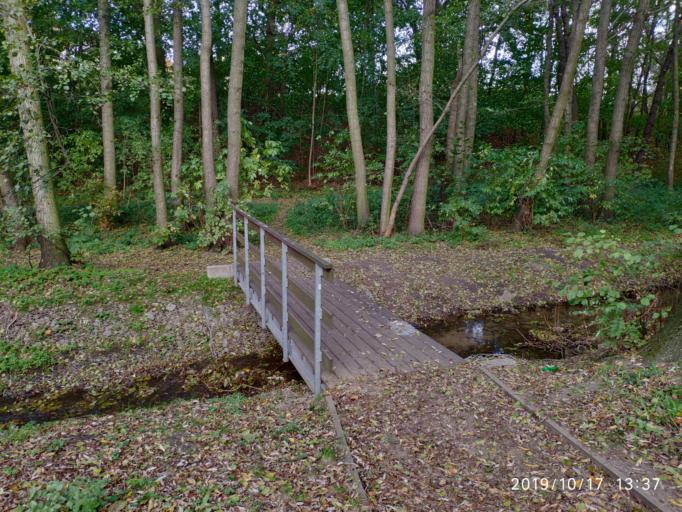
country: PL
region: Lubusz
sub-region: Zielona Gora
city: Zielona Gora
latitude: 51.9497
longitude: 15.5279
